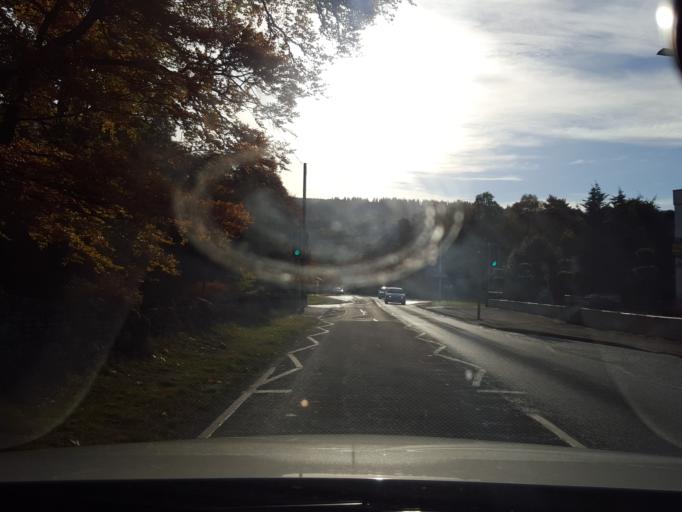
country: GB
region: Scotland
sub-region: Highland
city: Beauly
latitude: 57.3305
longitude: -4.4801
